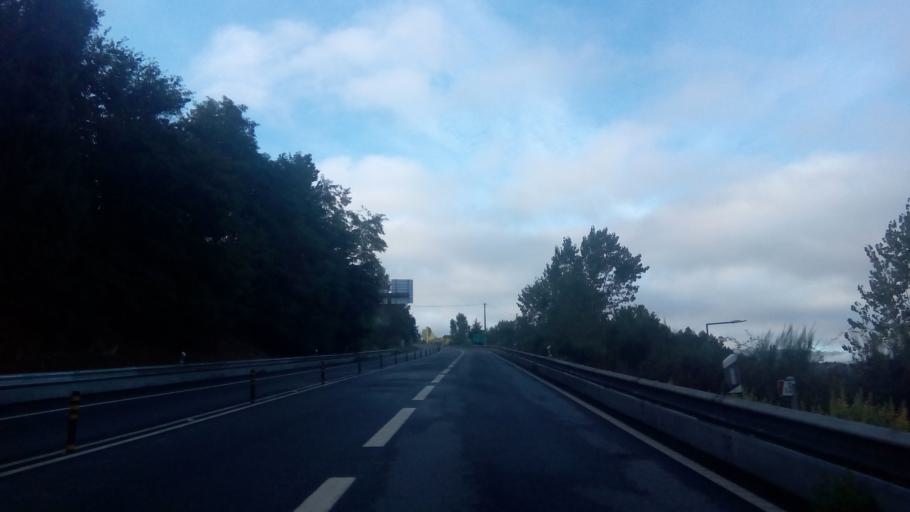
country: PT
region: Porto
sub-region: Amarante
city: Amarante
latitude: 41.2785
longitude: -7.9918
